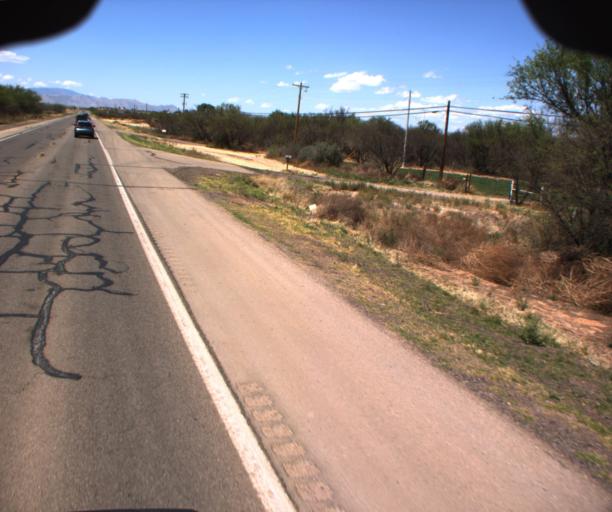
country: US
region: Arizona
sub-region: Cochise County
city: Saint David
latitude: 31.9107
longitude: -110.2585
